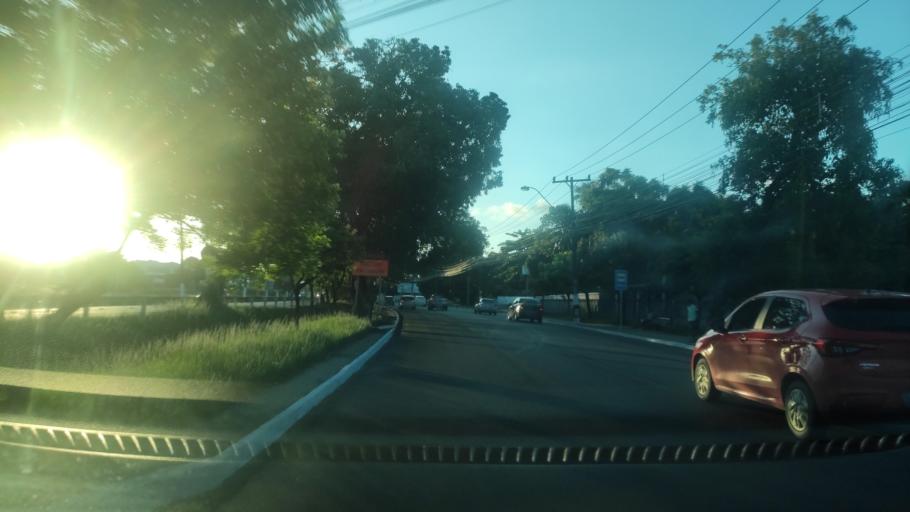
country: BR
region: Alagoas
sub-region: Maceio
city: Maceio
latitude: -9.5948
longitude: -35.7523
